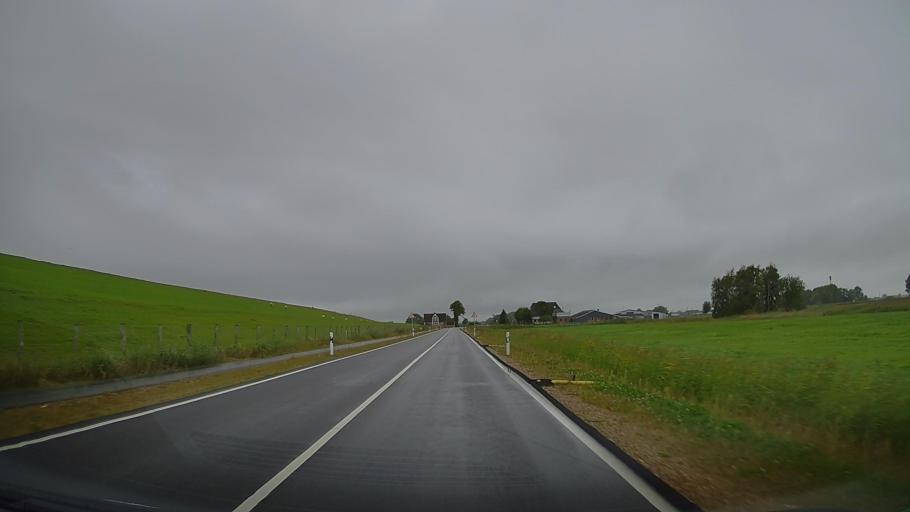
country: DE
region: Schleswig-Holstein
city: Brokdorf
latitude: 53.8730
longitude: 9.2950
